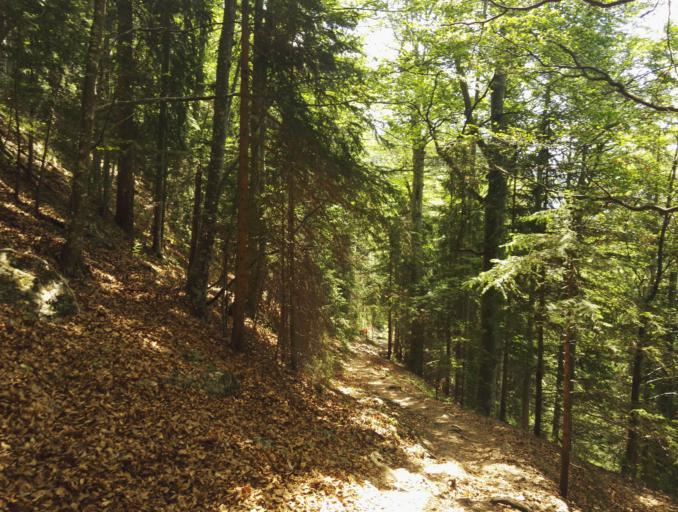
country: AT
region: Styria
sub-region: Politischer Bezirk Graz-Umgebung
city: Rothelstein
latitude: 47.3486
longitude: 15.3999
